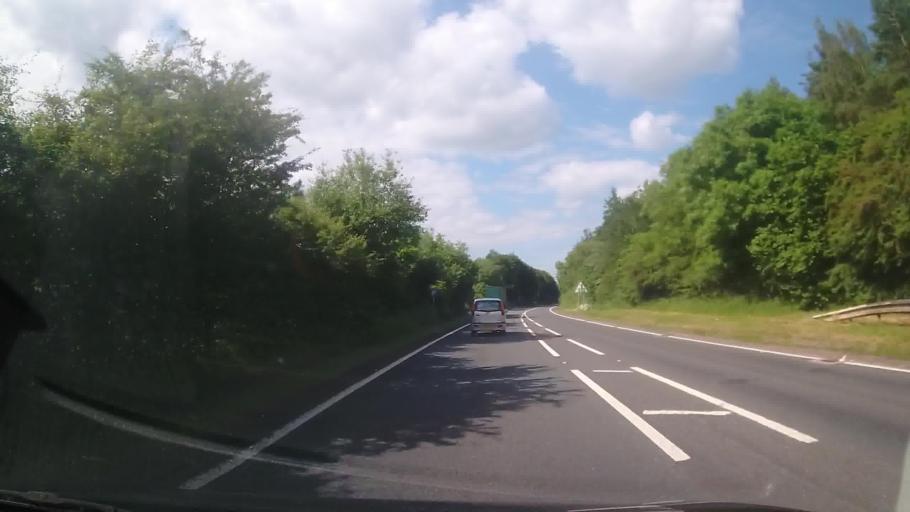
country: GB
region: England
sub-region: Herefordshire
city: Hope under Dinmore
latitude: 52.1929
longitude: -2.7194
